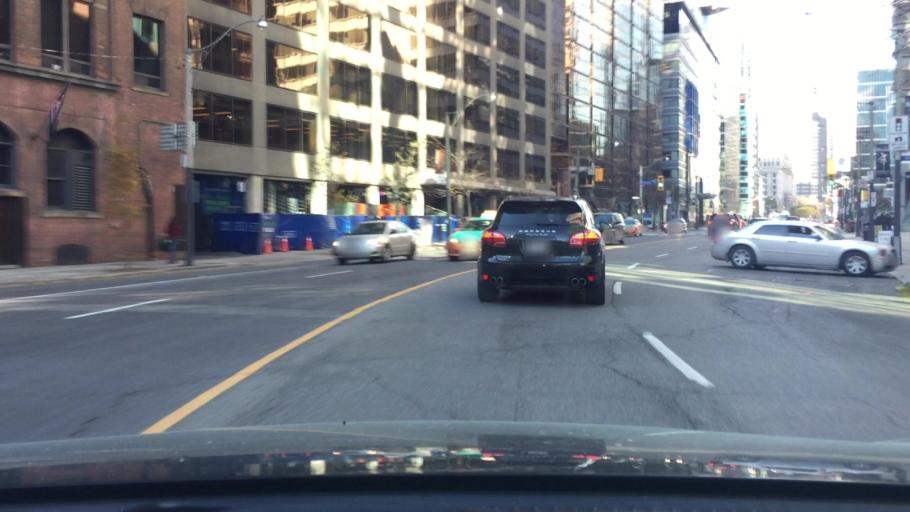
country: CA
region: Ontario
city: Toronto
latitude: 43.6457
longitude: -79.3836
